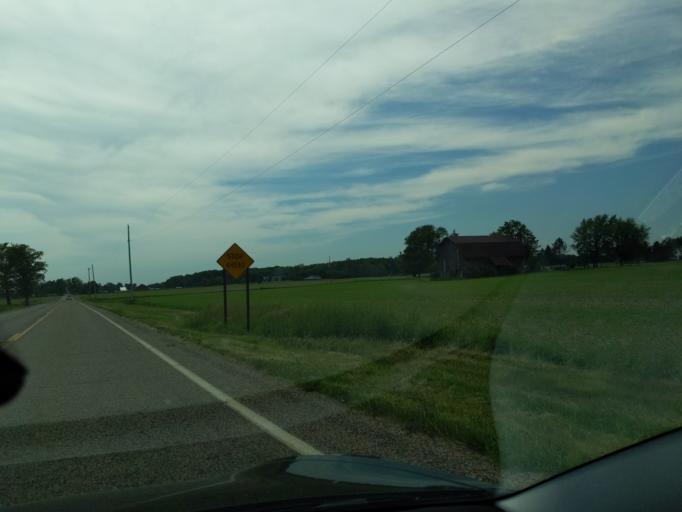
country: US
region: Michigan
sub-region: Barry County
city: Nashville
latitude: 42.7126
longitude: -85.0319
